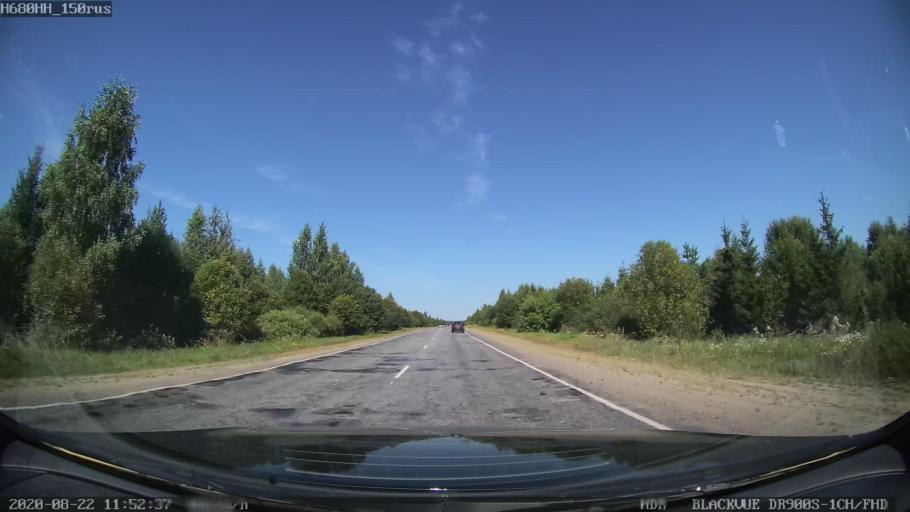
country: RU
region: Tverskaya
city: Vasil'yevskiy Mokh
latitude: 57.1177
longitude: 36.1158
